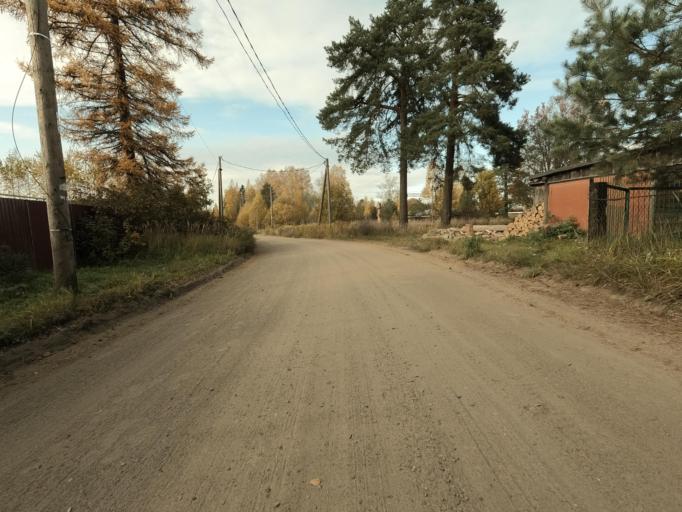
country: RU
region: Leningrad
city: Priladozhskiy
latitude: 59.6291
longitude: 31.4046
